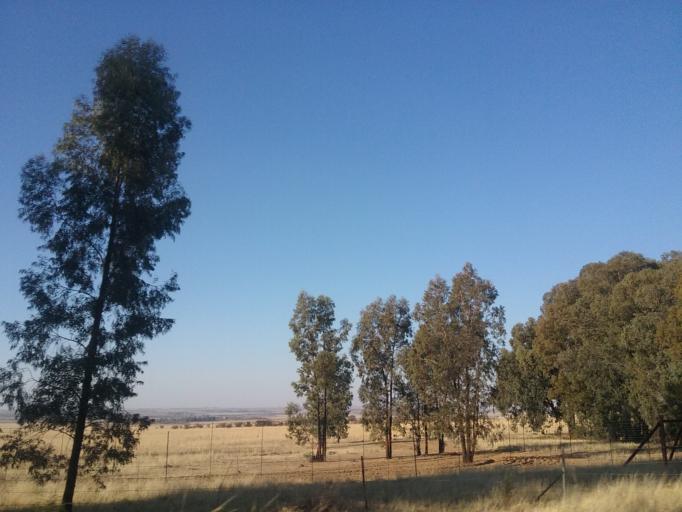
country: ZA
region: Orange Free State
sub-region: Fezile Dabi District Municipality
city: Kroonstad
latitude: -27.7862
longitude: 27.3205
